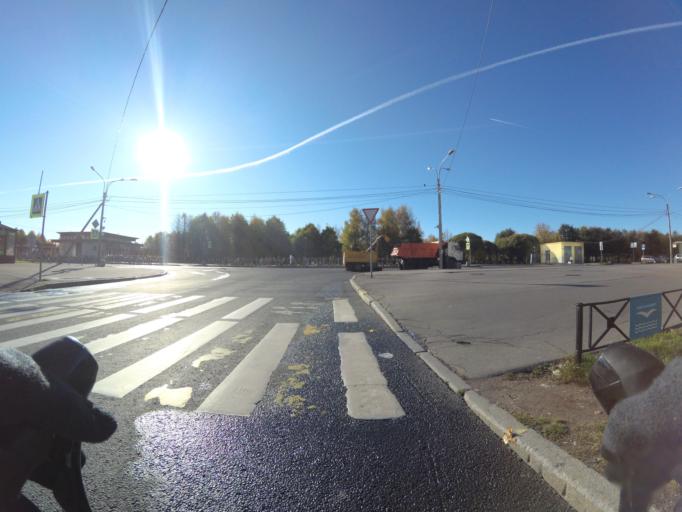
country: RU
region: Leningrad
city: Untolovo
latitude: 59.9850
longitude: 30.2008
